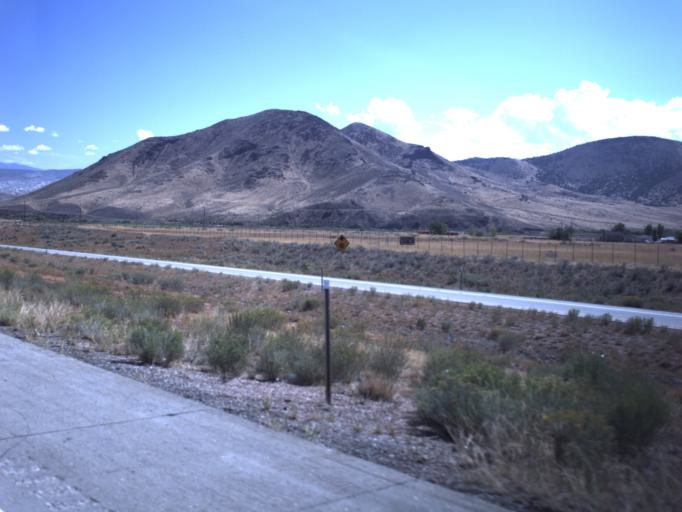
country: US
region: Utah
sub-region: Sevier County
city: Aurora
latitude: 38.8718
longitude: -111.9701
